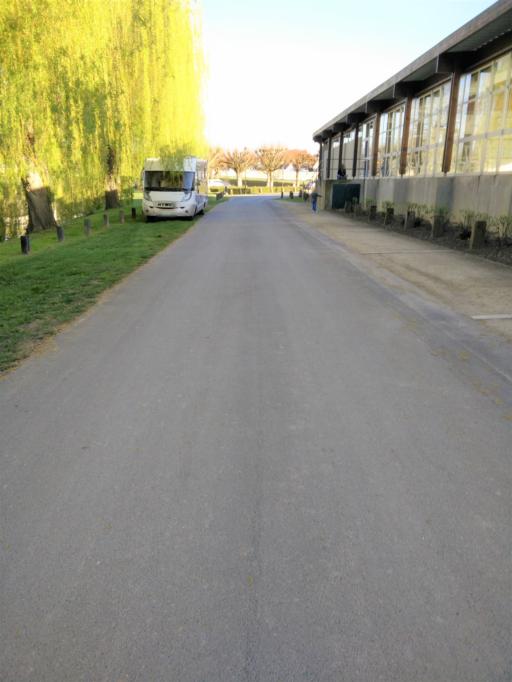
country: FR
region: Centre
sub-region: Departement du Loir-et-Cher
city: Saint-Aignan
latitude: 47.2724
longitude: 1.3738
